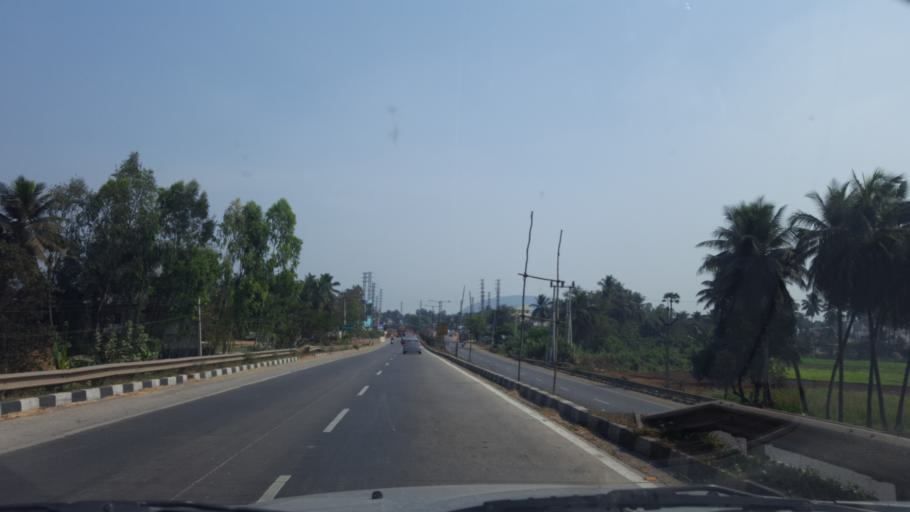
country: IN
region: Andhra Pradesh
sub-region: Vishakhapatnam
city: Anakapalle
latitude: 17.6784
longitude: 82.9939
